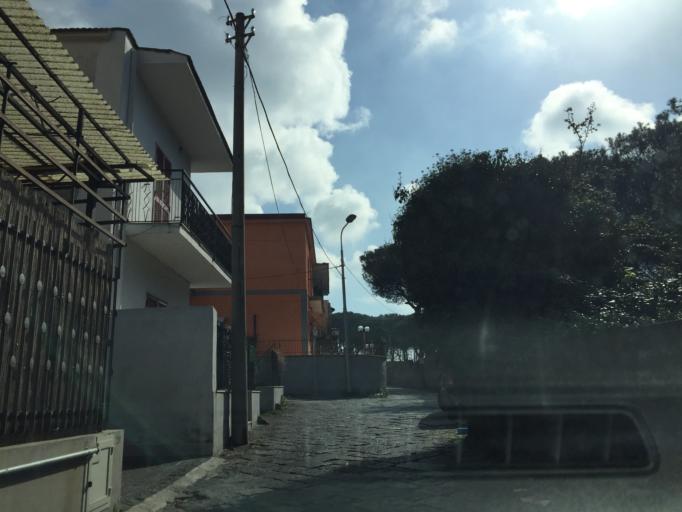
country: IT
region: Campania
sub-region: Provincia di Napoli
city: Torre del Greco
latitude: 40.7797
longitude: 14.4096
